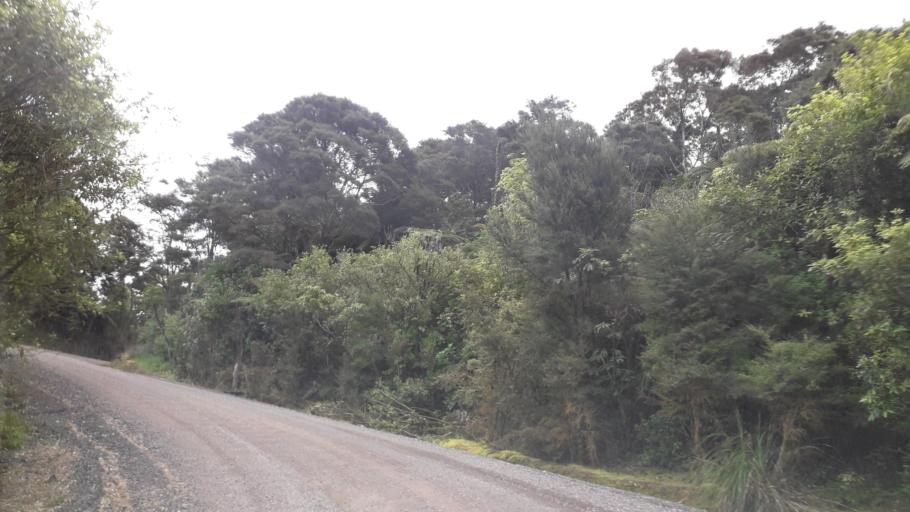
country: NZ
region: Northland
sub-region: Far North District
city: Paihia
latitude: -35.3186
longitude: 174.2324
